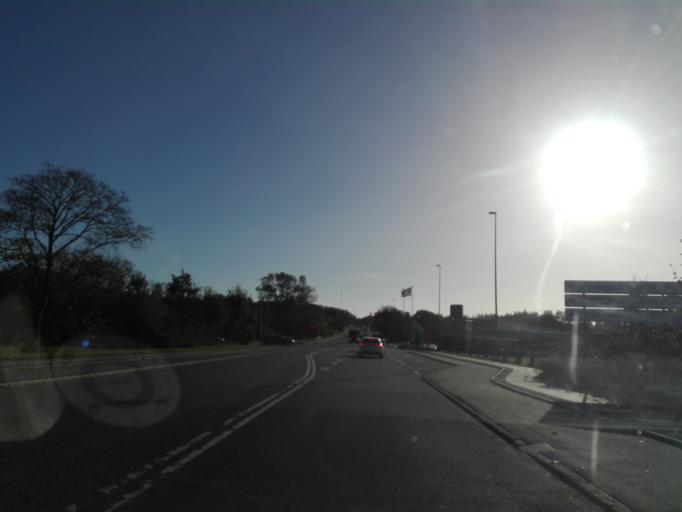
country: DK
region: Central Jutland
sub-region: Arhus Kommune
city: Beder
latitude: 56.1083
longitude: 10.2079
